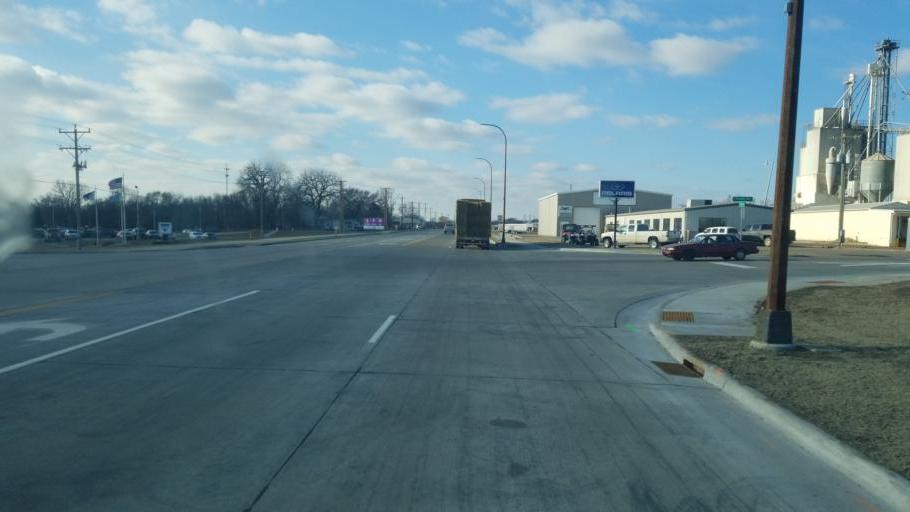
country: US
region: South Dakota
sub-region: Yankton County
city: Yankton
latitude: 42.8773
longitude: -97.3684
